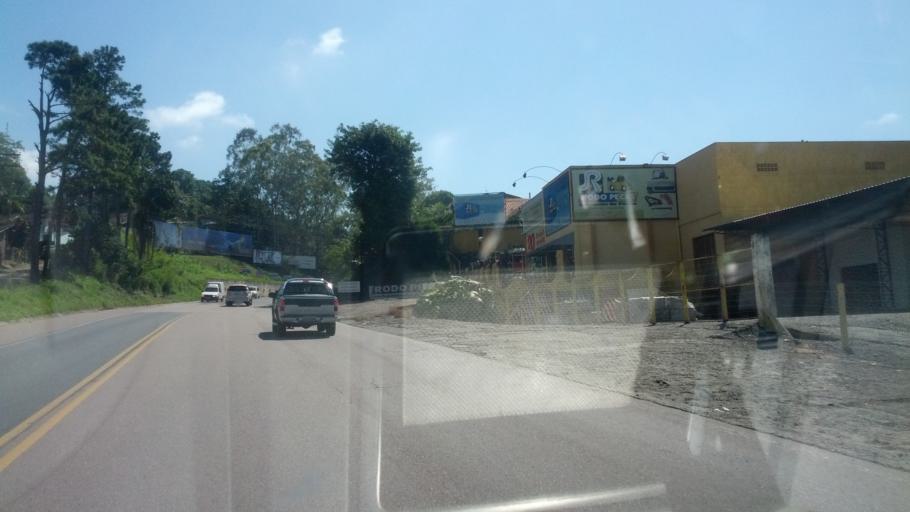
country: BR
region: Santa Catarina
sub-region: Rio Do Sul
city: Rio do Sul
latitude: -27.2062
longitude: -49.6468
